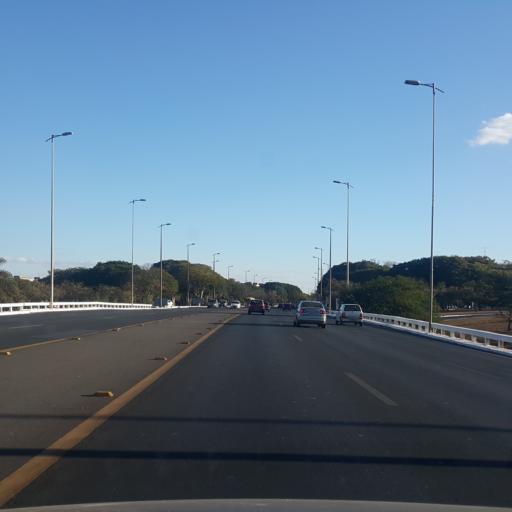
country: BR
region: Federal District
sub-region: Brasilia
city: Brasilia
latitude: -15.8002
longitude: -47.8853
